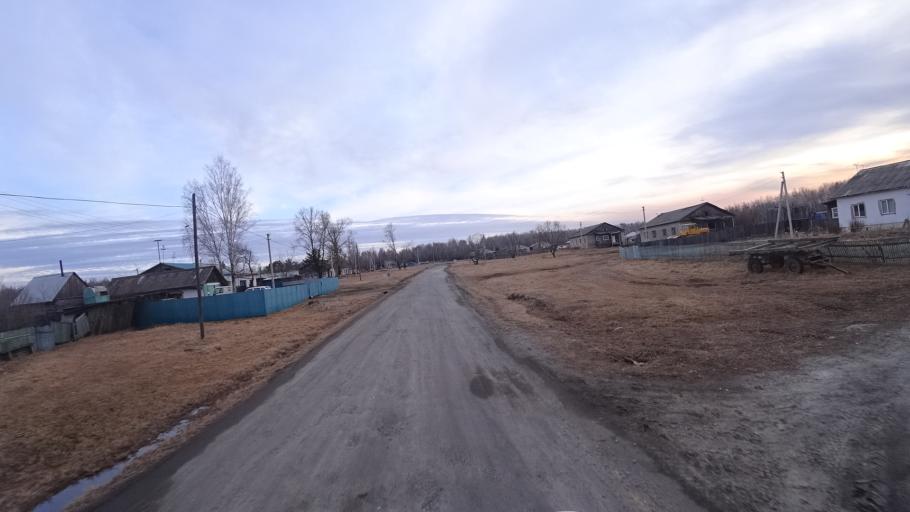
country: RU
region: Amur
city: Bureya
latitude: 50.0175
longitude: 129.7682
